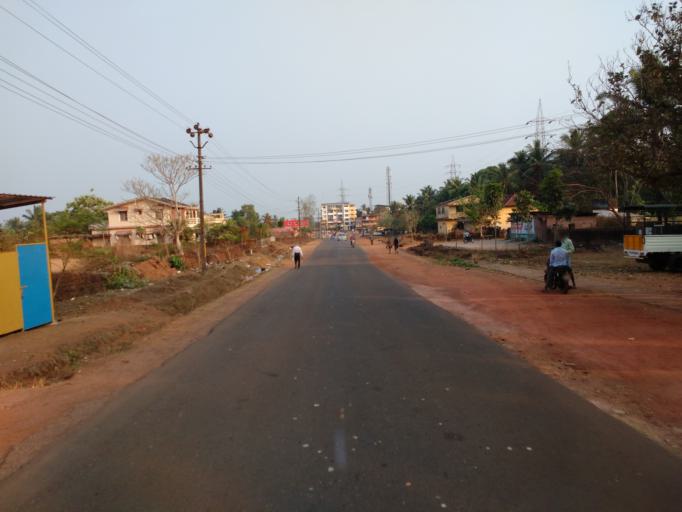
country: IN
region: Karnataka
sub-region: Dakshina Kannada
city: Mangalore
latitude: 12.9189
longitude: 74.8992
